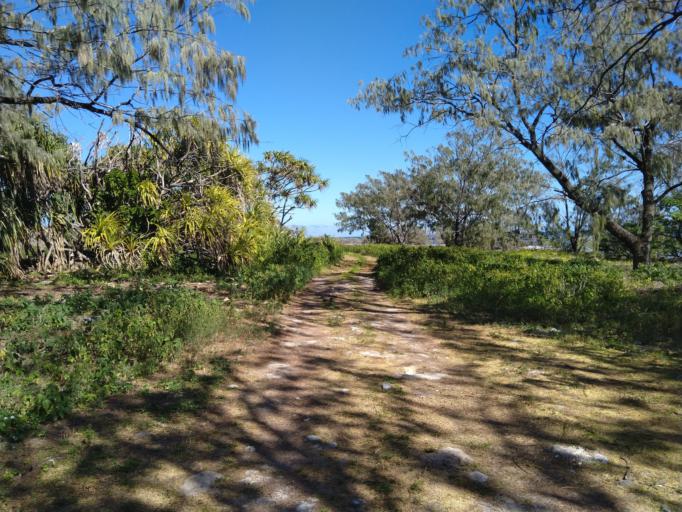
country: AU
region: Queensland
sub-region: Bundaberg
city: Bundaberg
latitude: -24.1103
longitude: 152.7143
